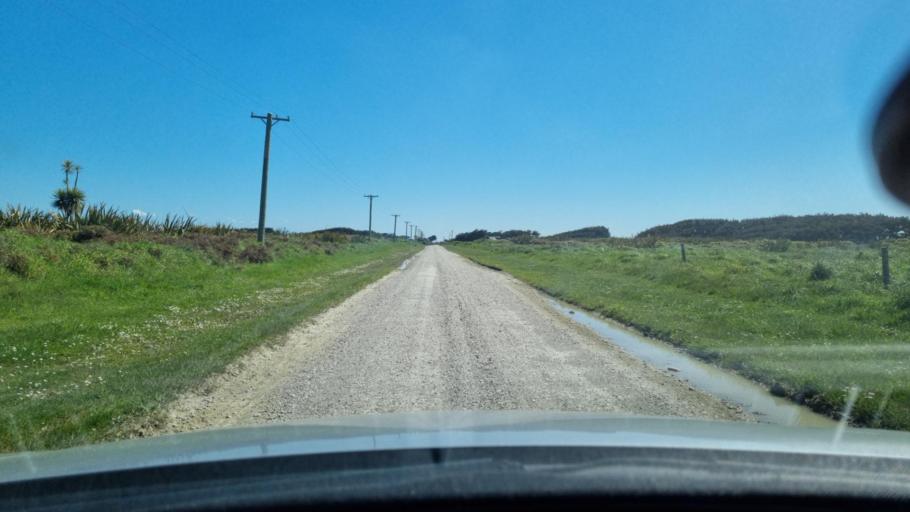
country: NZ
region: Southland
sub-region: Invercargill City
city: Invercargill
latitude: -46.4342
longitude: 168.2365
